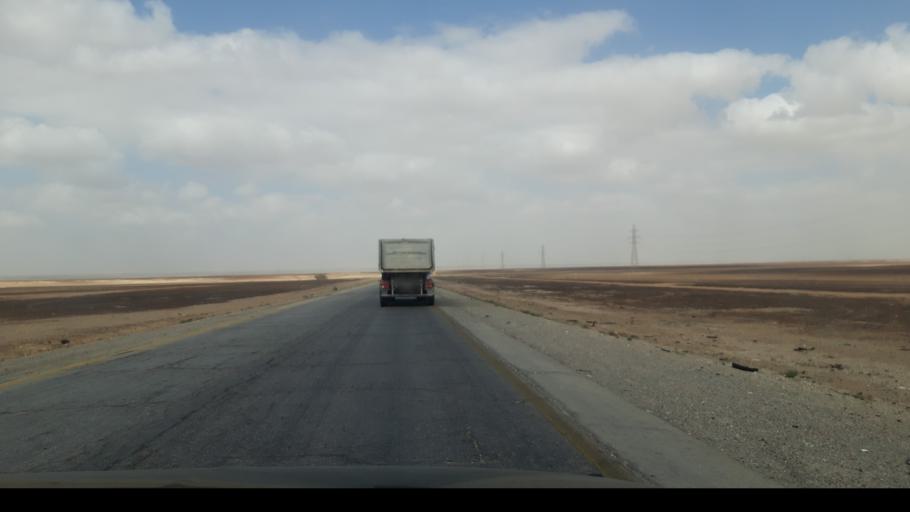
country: JO
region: Amman
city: Al Azraq ash Shamali
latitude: 31.7739
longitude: 36.5666
